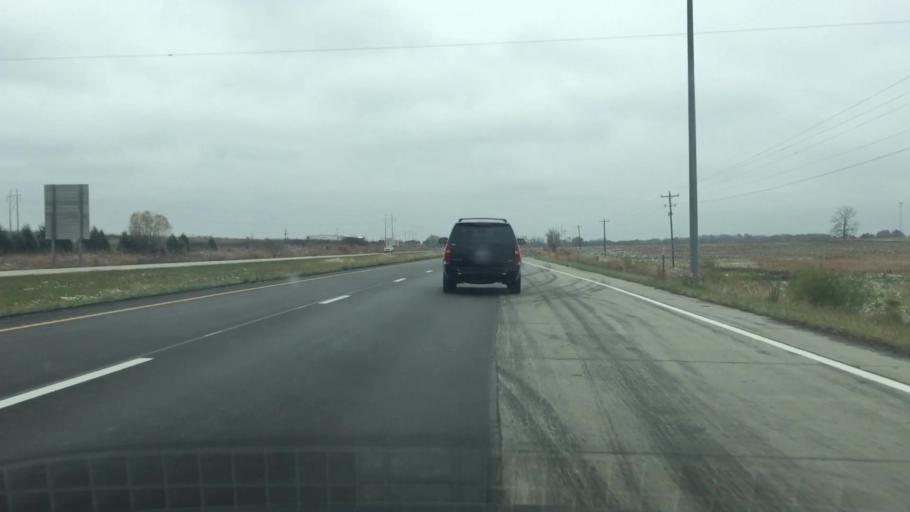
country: US
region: Missouri
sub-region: Saint Clair County
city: Osceola
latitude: 38.0368
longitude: -93.6798
